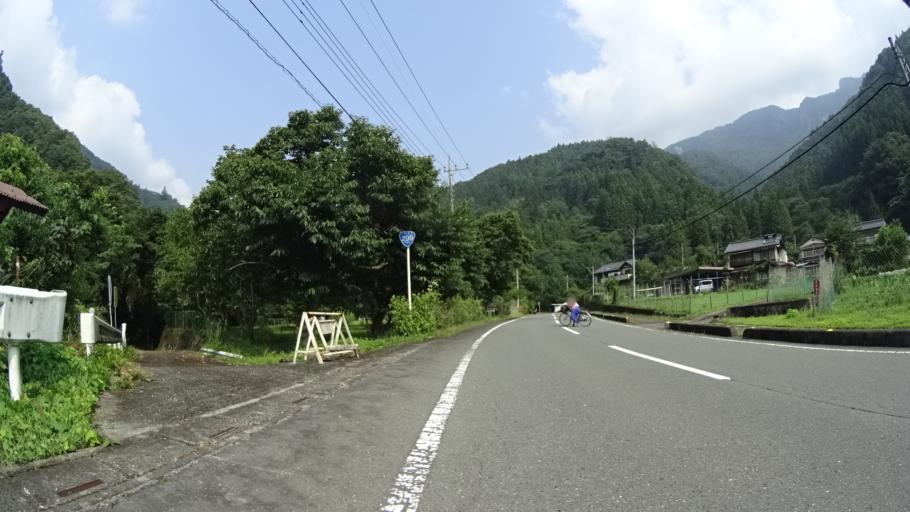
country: JP
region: Saitama
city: Chichibu
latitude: 36.0370
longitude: 138.9148
